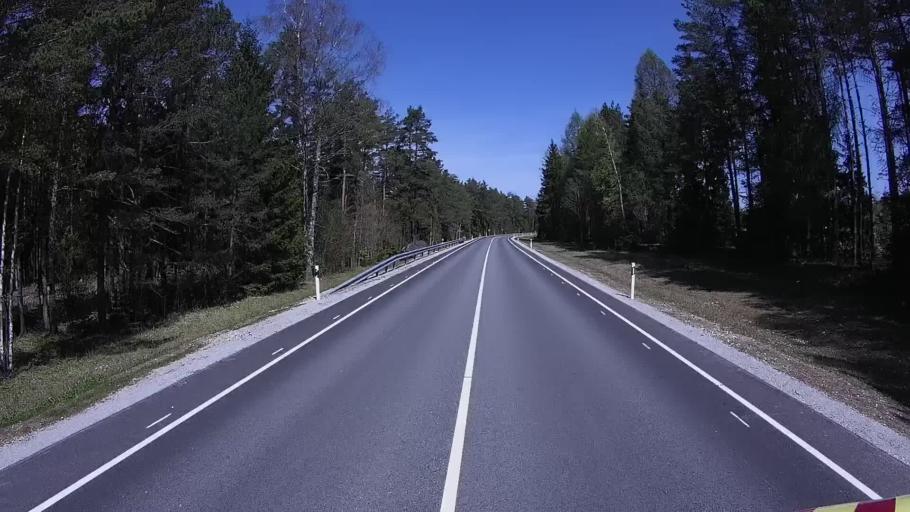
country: EE
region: Laeaene
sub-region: Ridala Parish
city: Uuemoisa
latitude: 59.0391
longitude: 23.8294
